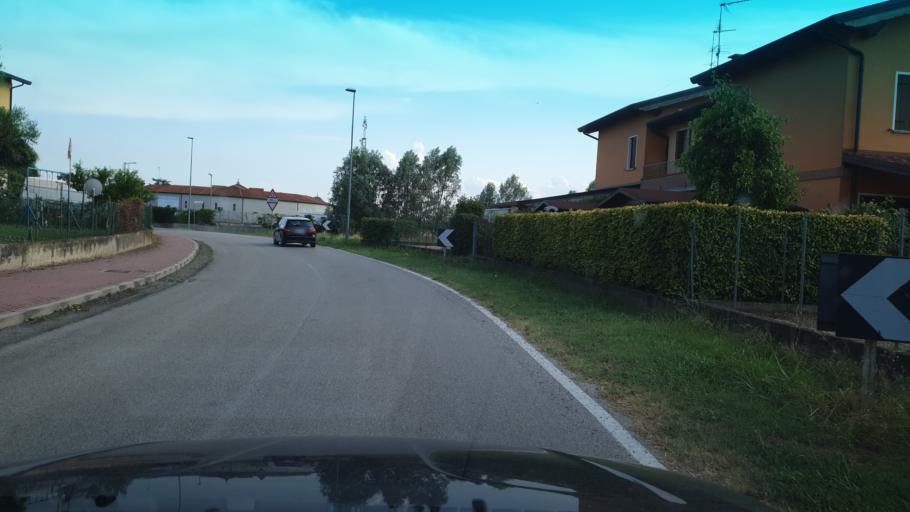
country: IT
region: Veneto
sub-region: Provincia di Rovigo
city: Castelguglielmo
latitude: 45.0235
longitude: 11.5351
